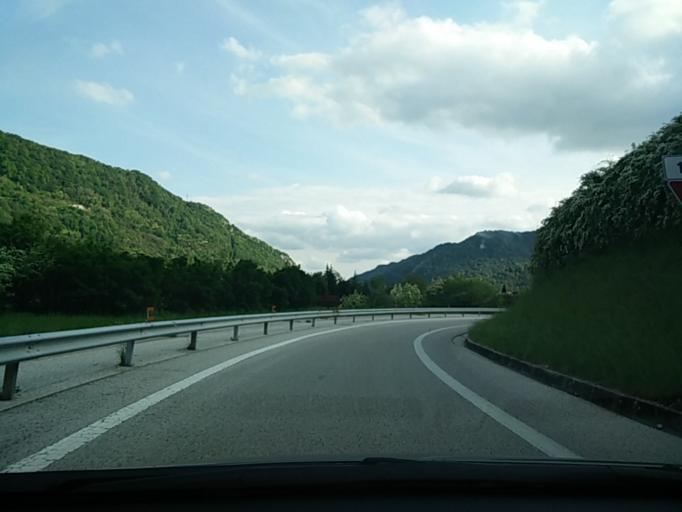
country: IT
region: Veneto
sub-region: Provincia di Treviso
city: Revine
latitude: 46.0173
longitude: 12.2848
